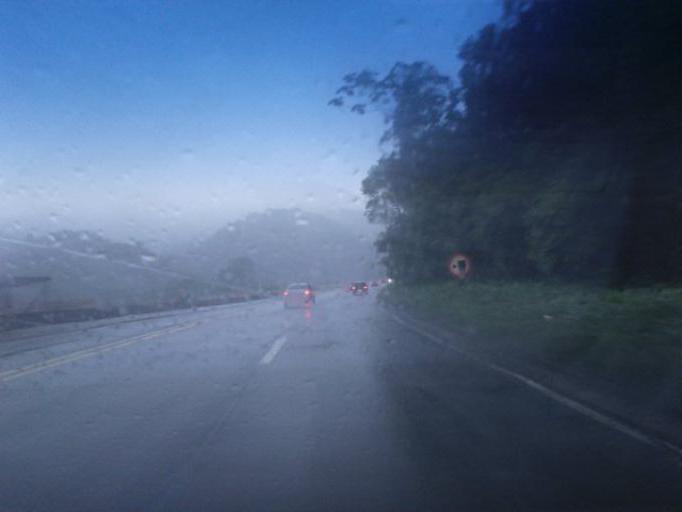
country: BR
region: Sao Paulo
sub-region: Juquitiba
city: Juquitiba
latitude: -24.0773
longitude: -47.2512
